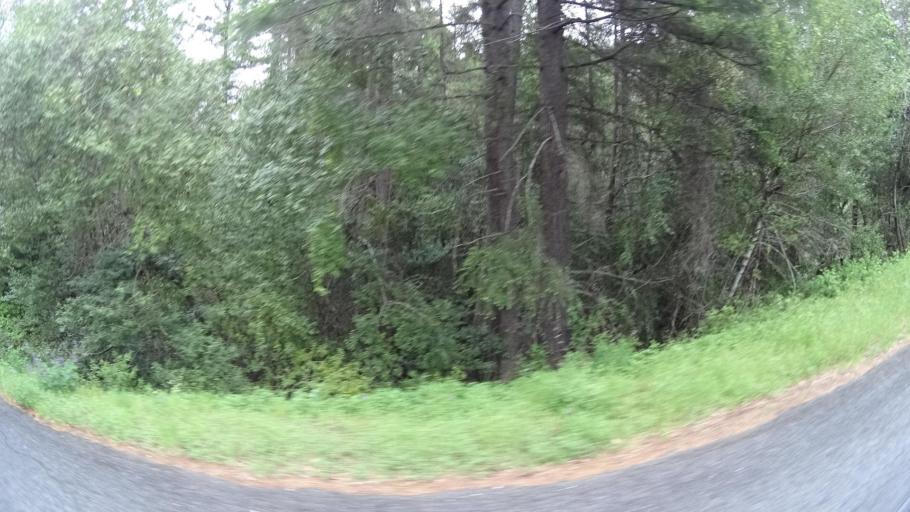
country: US
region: California
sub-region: Humboldt County
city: Willow Creek
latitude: 41.3241
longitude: -123.5255
